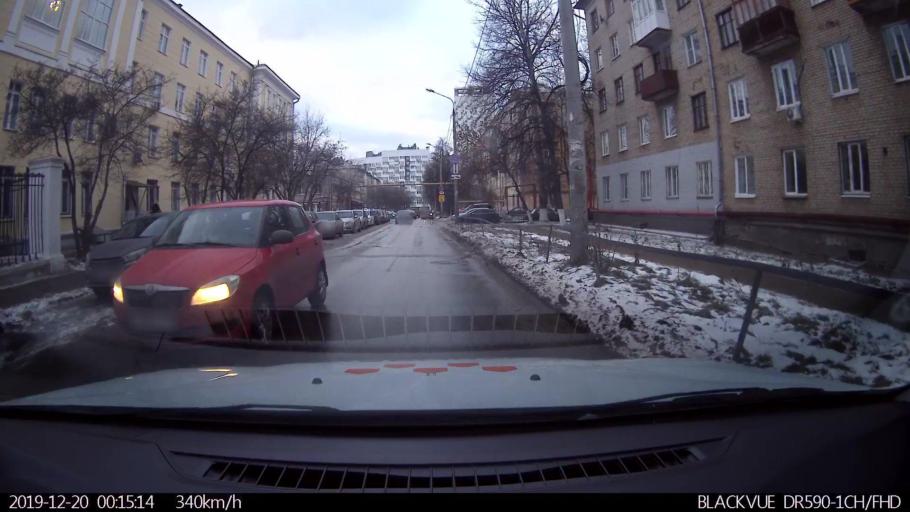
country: RU
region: Jaroslavl
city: Porech'ye-Rybnoye
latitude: 56.9976
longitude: 39.3905
